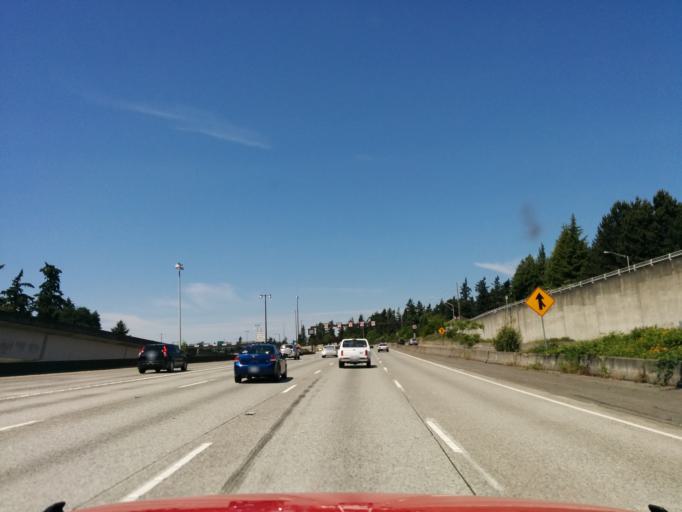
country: US
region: Washington
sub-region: King County
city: Newport
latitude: 47.5796
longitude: -122.1908
